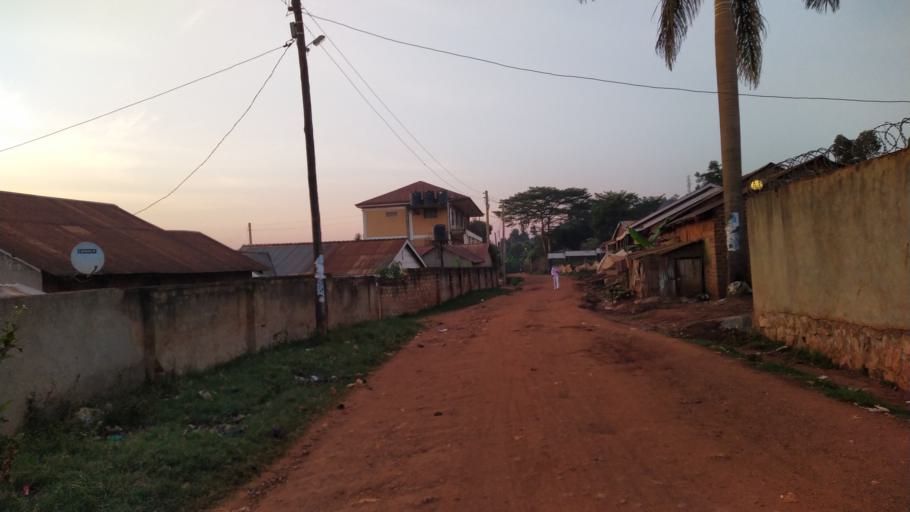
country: UG
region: Central Region
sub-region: Kampala District
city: Kampala
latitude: 0.2726
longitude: 32.5742
